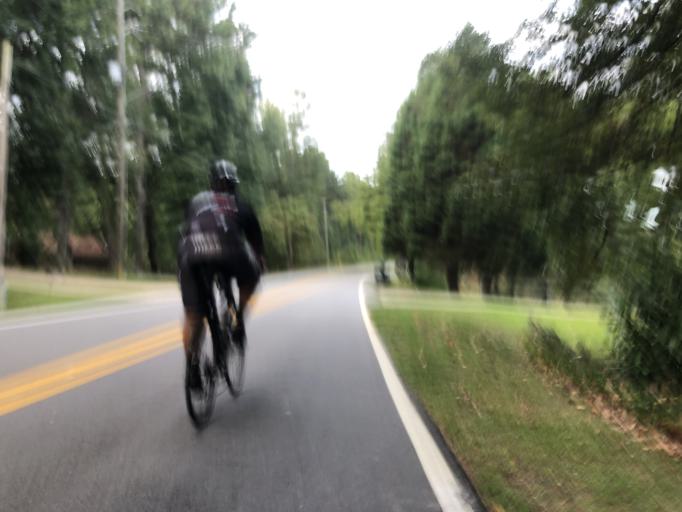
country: US
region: Georgia
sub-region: Fulton County
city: Fairburn
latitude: 33.6273
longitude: -84.6567
